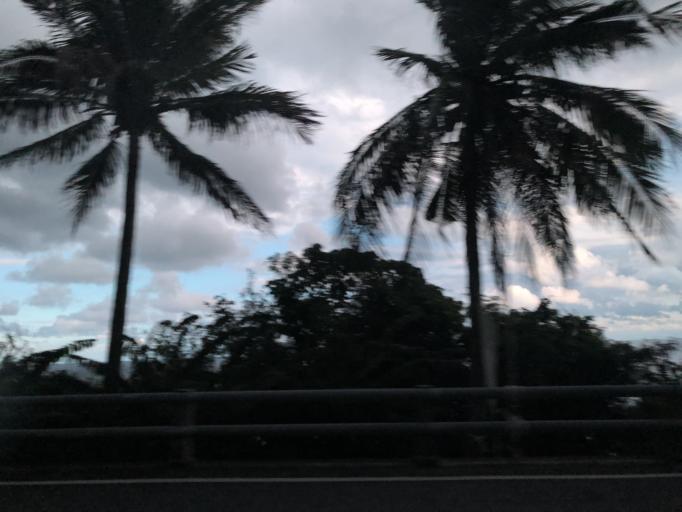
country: TW
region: Taiwan
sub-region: Taitung
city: Taitung
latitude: 22.8593
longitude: 121.1996
